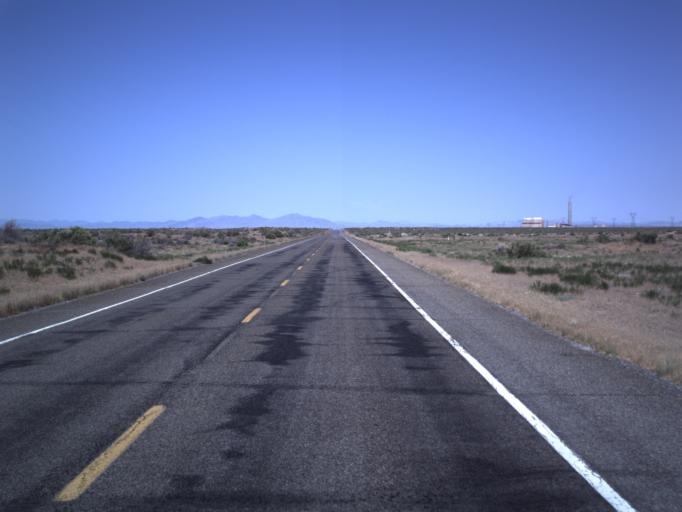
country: US
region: Utah
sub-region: Millard County
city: Delta
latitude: 39.4806
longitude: -112.5104
